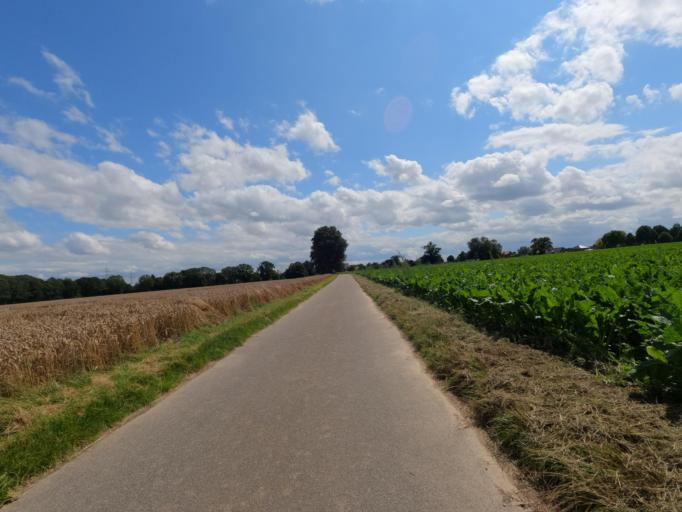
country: DE
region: North Rhine-Westphalia
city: Baesweiler
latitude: 50.9416
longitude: 6.2043
